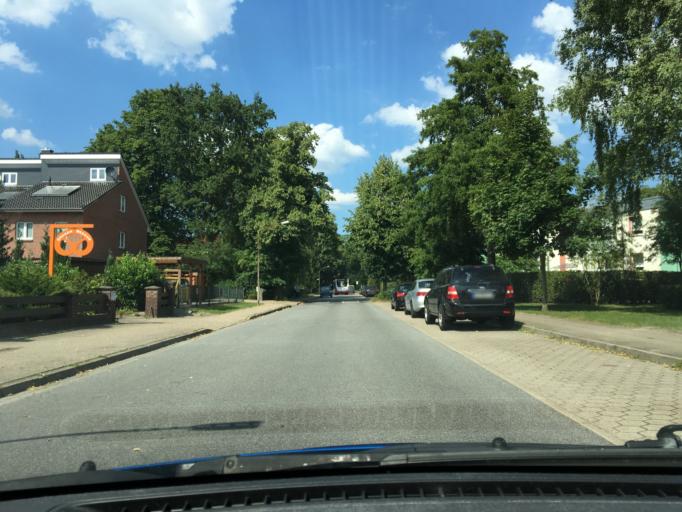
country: DE
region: Lower Saxony
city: Stelle
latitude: 53.4013
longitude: 10.0494
